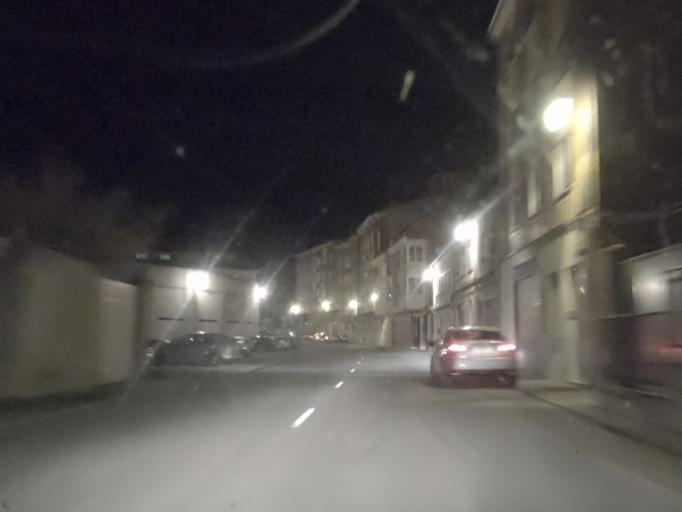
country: ES
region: Castille and Leon
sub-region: Provincia de Zamora
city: Benavente
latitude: 42.0061
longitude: -5.6836
